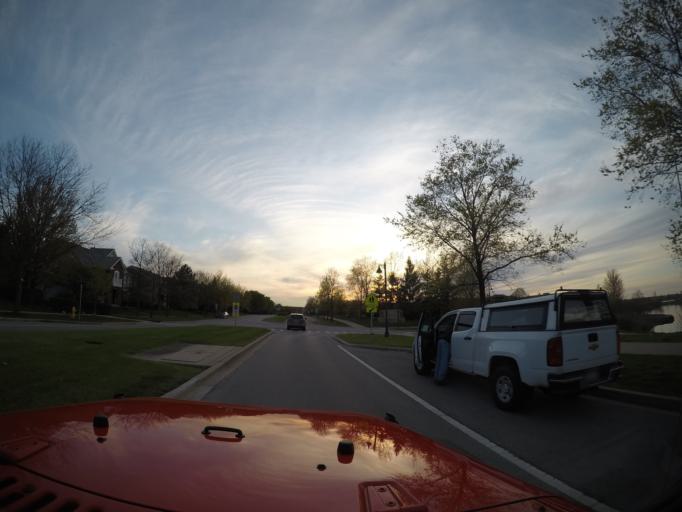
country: US
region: Illinois
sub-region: Cook County
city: Glenview
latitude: 42.0874
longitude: -87.8154
